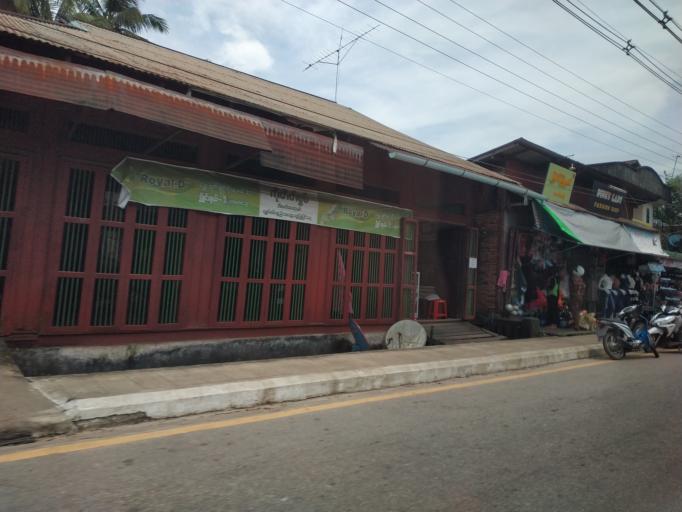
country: MM
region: Tanintharyi
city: Dawei
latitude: 14.0735
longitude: 98.2008
